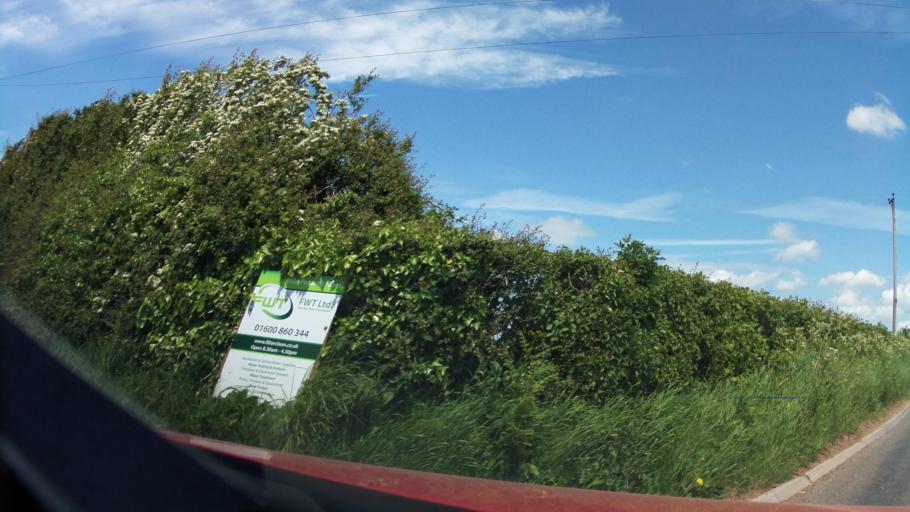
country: GB
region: Wales
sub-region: Monmouthshire
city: Mitchel Troy
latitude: 51.7295
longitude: -2.7518
